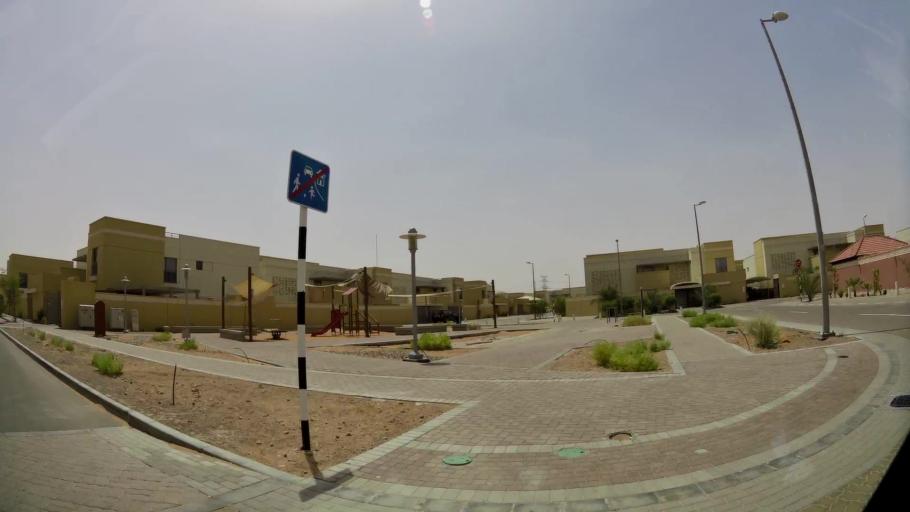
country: AE
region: Abu Dhabi
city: Al Ain
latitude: 24.1440
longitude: 55.6271
